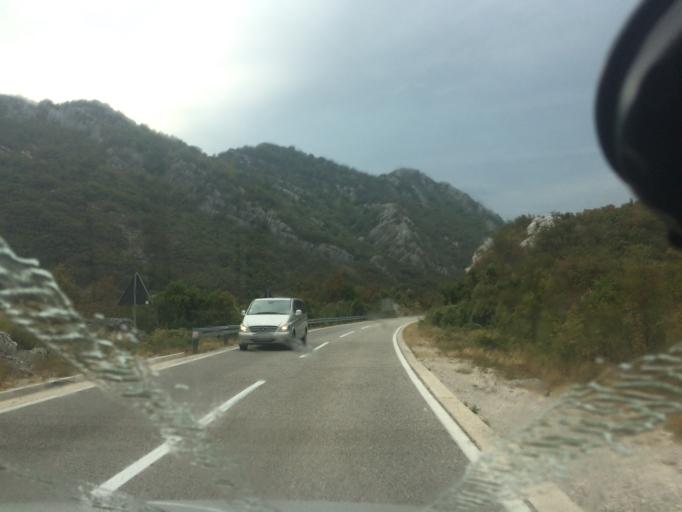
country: ME
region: Kotor
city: Risan
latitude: 42.5691
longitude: 18.6905
